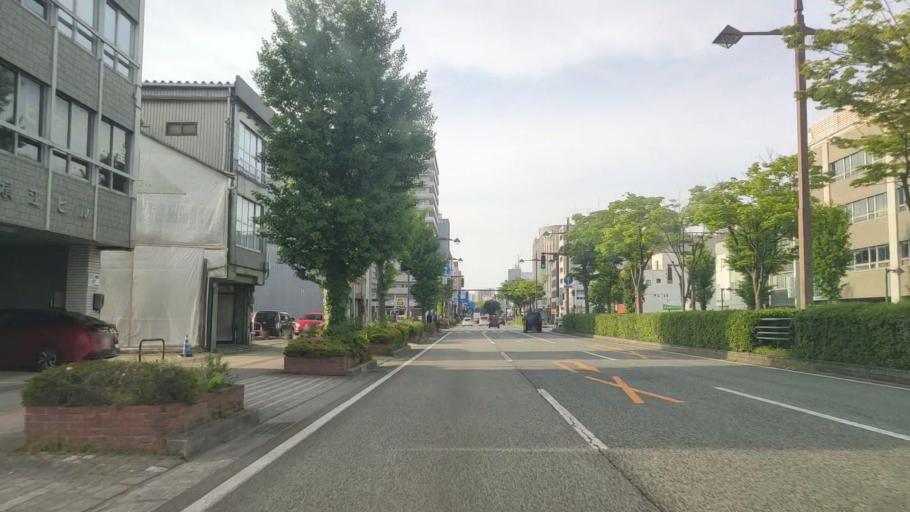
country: JP
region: Toyama
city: Toyama-shi
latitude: 36.6866
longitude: 137.2120
